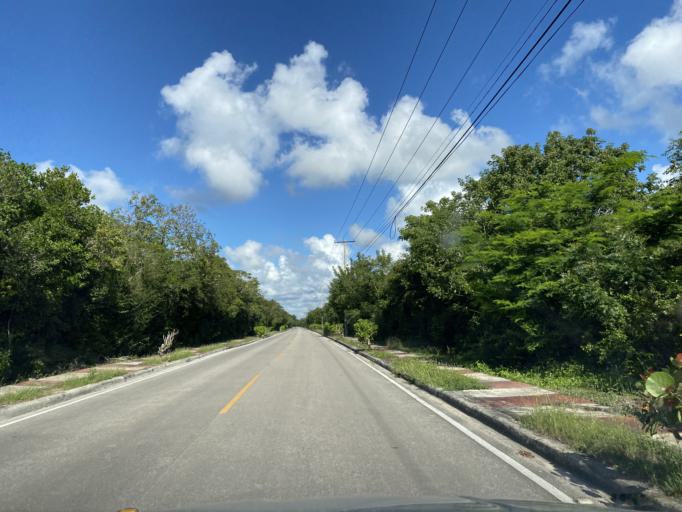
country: DO
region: La Altagracia
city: San Rafael del Yuma
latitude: 18.3368
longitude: -68.8101
